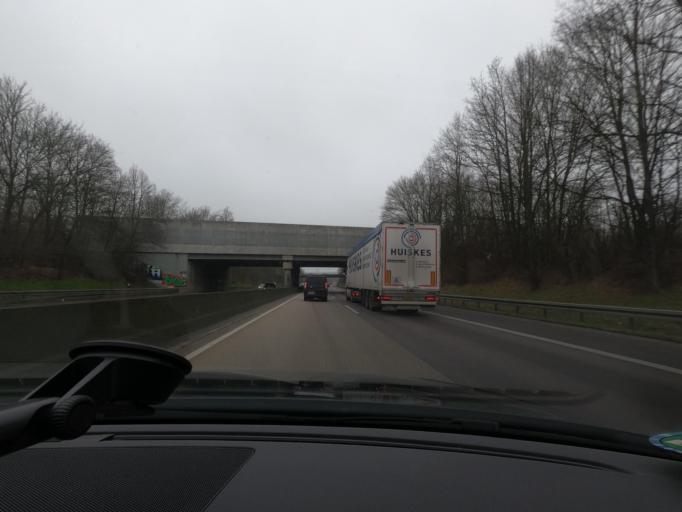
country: DE
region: North Rhine-Westphalia
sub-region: Regierungsbezirk Koln
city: Bedburg
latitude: 50.9659
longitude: 6.5668
